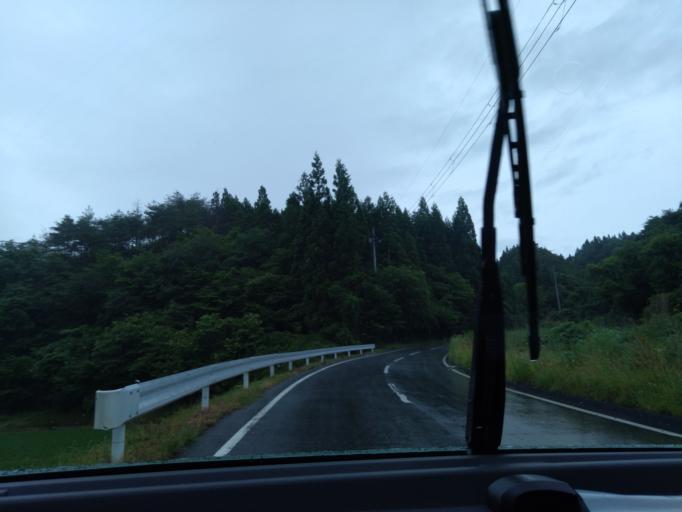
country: JP
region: Iwate
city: Ichinoseki
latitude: 38.8638
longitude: 141.0266
